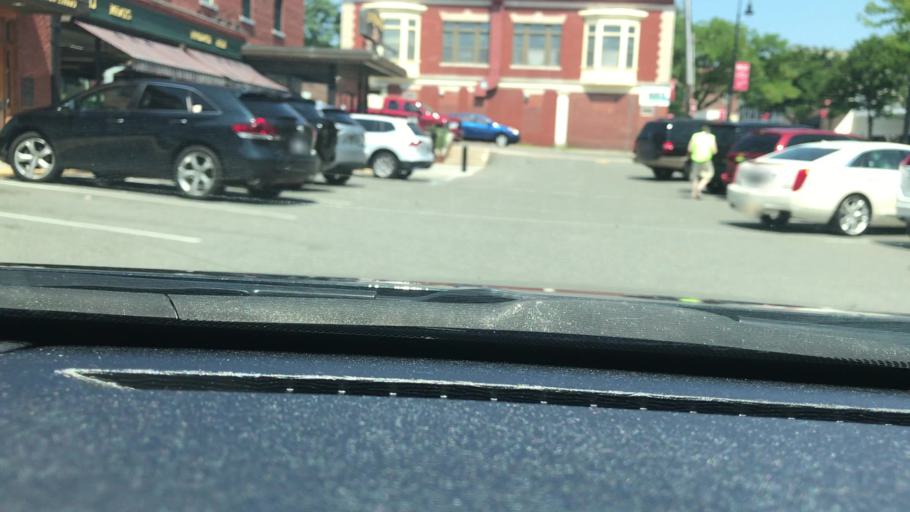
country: US
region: Massachusetts
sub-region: Middlesex County
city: Wakefield
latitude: 42.5023
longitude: -71.0700
